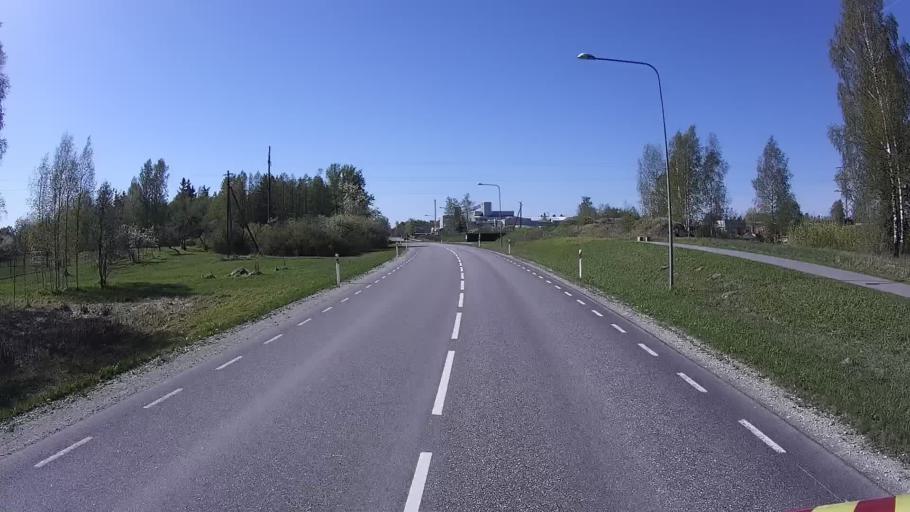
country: EE
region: Raplamaa
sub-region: Jaervakandi vald
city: Jarvakandi
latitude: 58.7830
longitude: 24.8181
